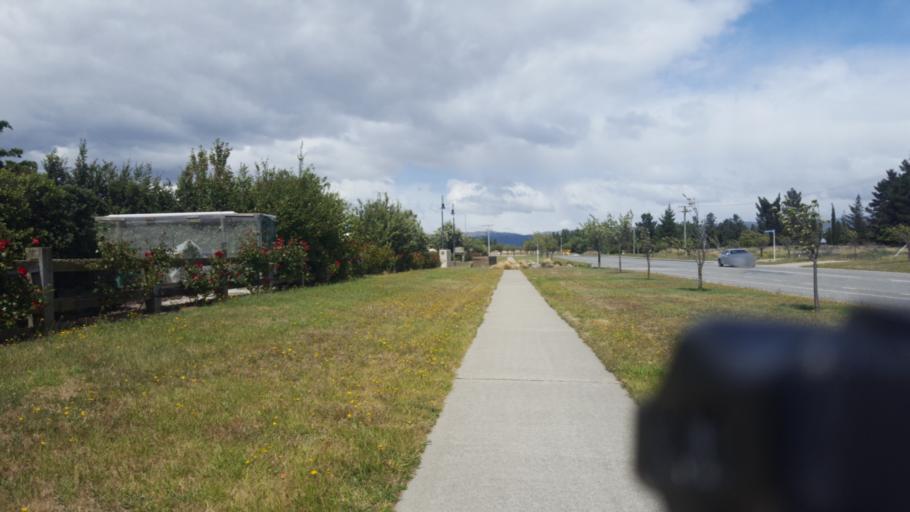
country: NZ
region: Otago
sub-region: Queenstown-Lakes District
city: Wanaka
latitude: -45.1970
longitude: 169.3301
